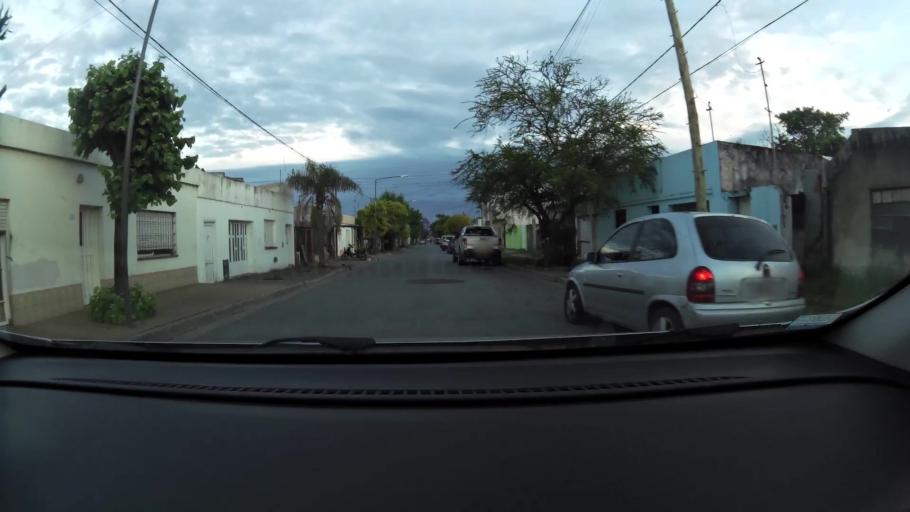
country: AR
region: Buenos Aires
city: San Nicolas de los Arroyos
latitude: -33.3250
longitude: -60.2316
